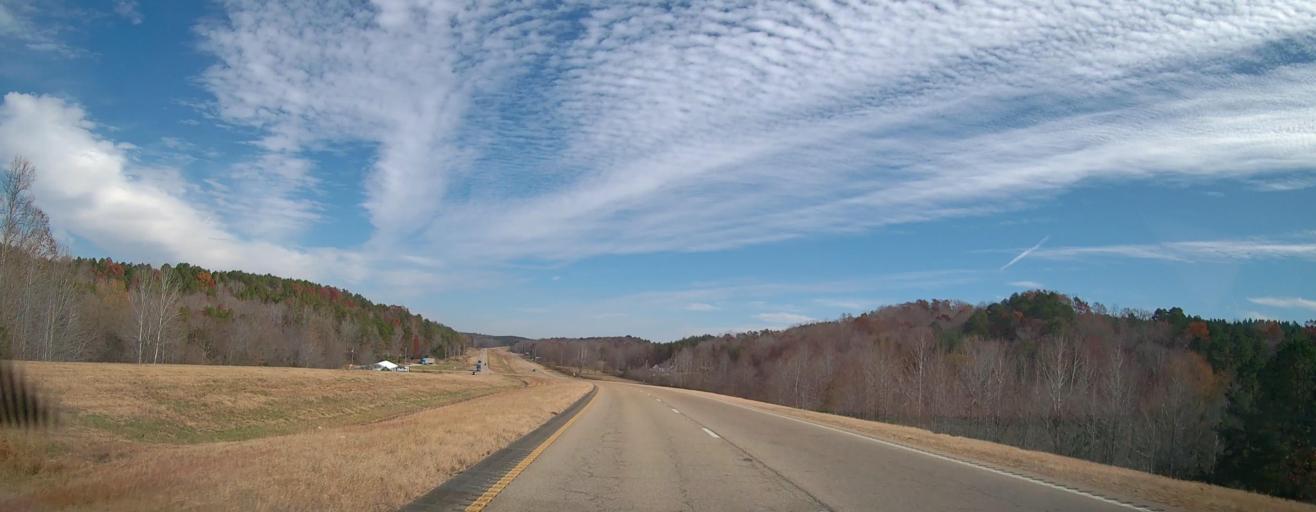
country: US
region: Mississippi
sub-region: Alcorn County
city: Corinth
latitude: 34.9318
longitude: -88.7592
